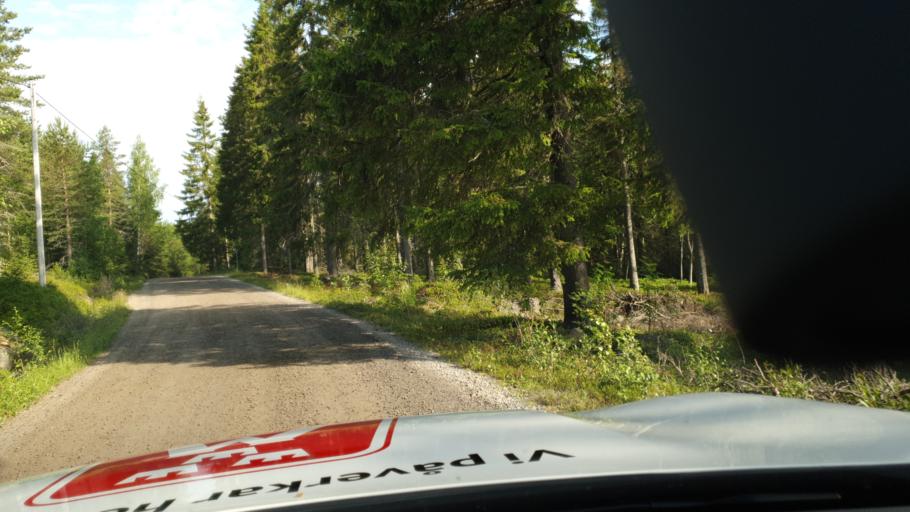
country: SE
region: Vaesterbotten
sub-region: Robertsfors Kommun
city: Robertsfors
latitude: 64.2155
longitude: 21.0774
